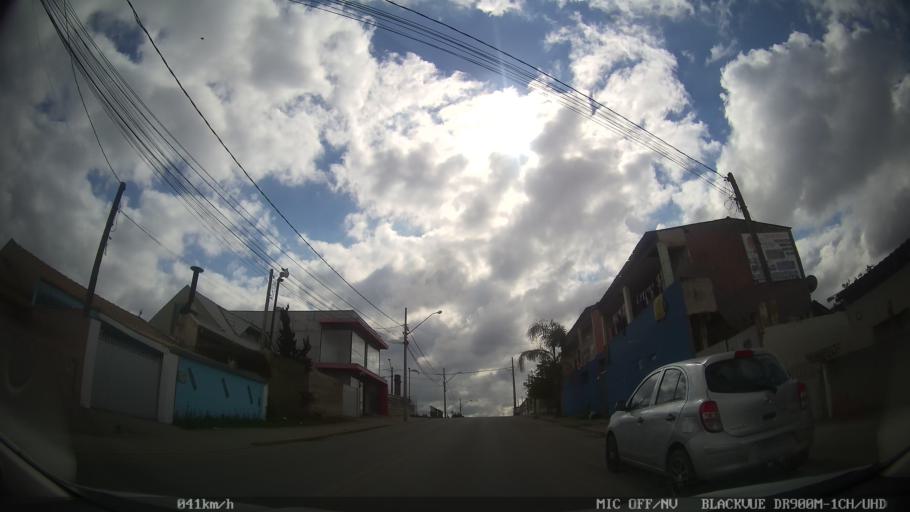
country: BR
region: Parana
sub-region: Pinhais
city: Pinhais
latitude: -25.3754
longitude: -49.2006
